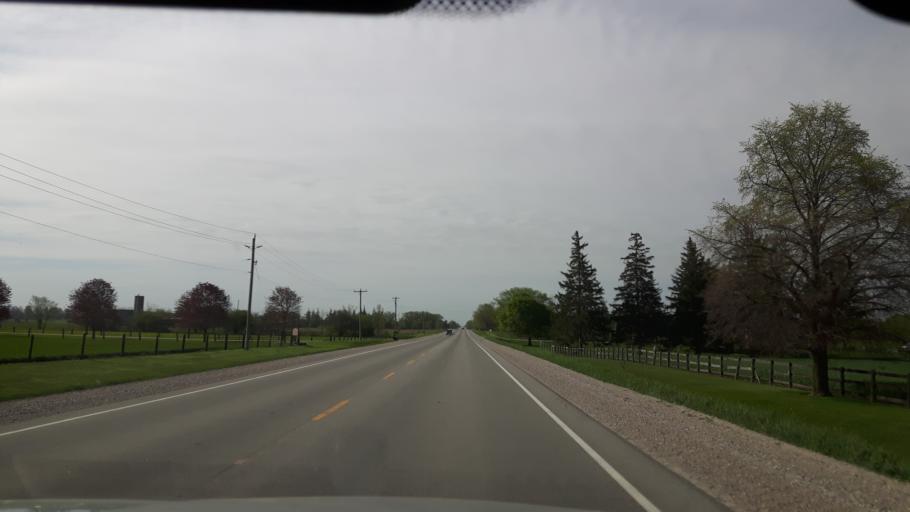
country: CA
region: Ontario
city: Bluewater
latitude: 43.4266
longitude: -81.4970
